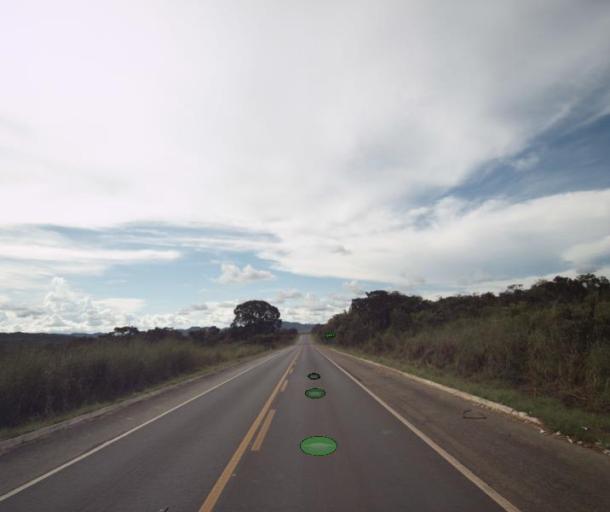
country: BR
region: Goias
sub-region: Barro Alto
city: Barro Alto
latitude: -15.2019
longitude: -48.7016
